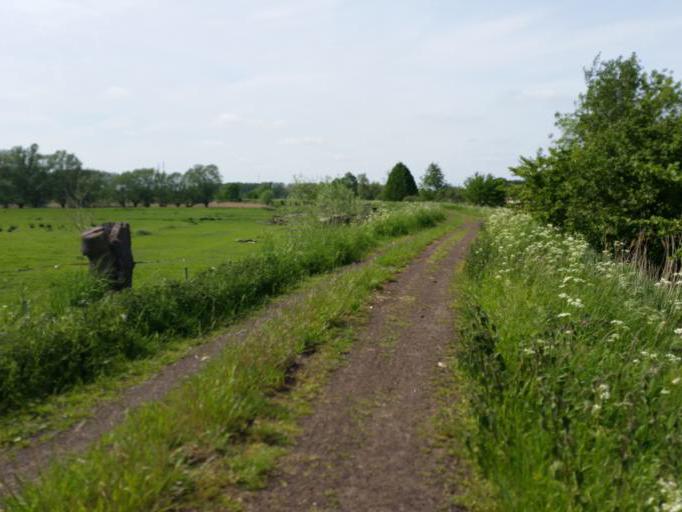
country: BE
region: Flanders
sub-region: Provincie Antwerpen
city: Niel
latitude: 51.1009
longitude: 4.3267
